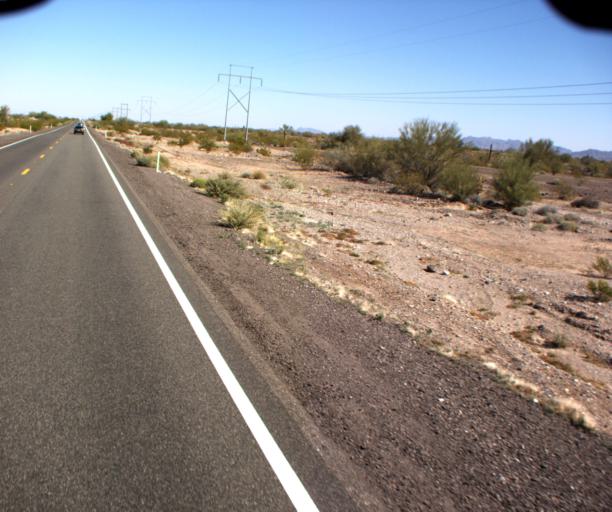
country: US
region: Arizona
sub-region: La Paz County
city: Quartzsite
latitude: 33.5673
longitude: -114.2170
